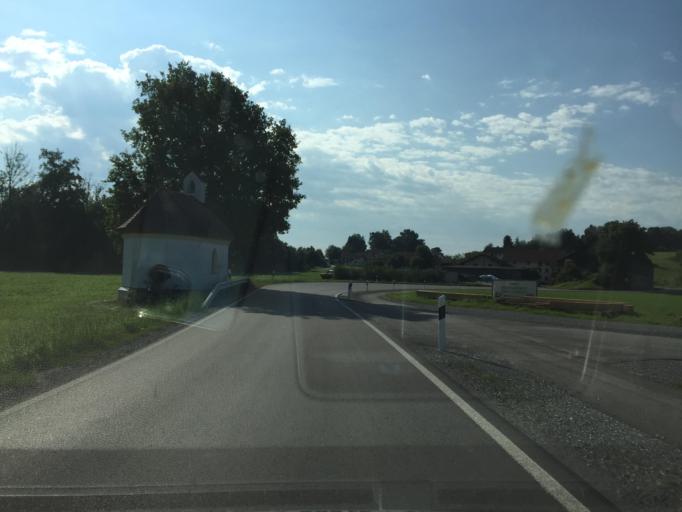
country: DE
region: Bavaria
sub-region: Upper Bavaria
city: Tuntenhausen
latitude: 47.9537
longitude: 12.0197
